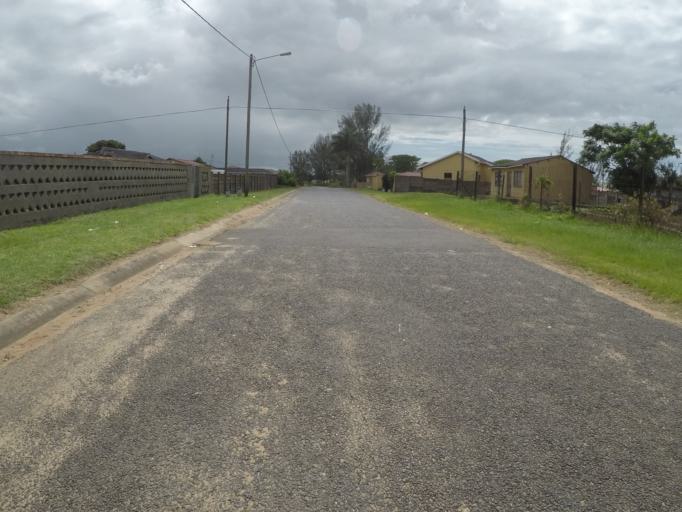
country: ZA
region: KwaZulu-Natal
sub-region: uThungulu District Municipality
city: eSikhawini
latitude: -28.8641
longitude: 31.9160
